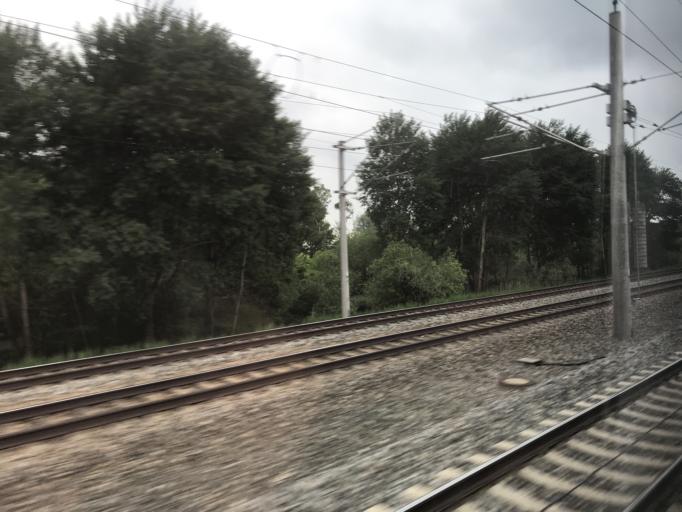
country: DE
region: Bavaria
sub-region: Upper Bavaria
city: Mammendorf
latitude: 48.2178
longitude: 11.1446
